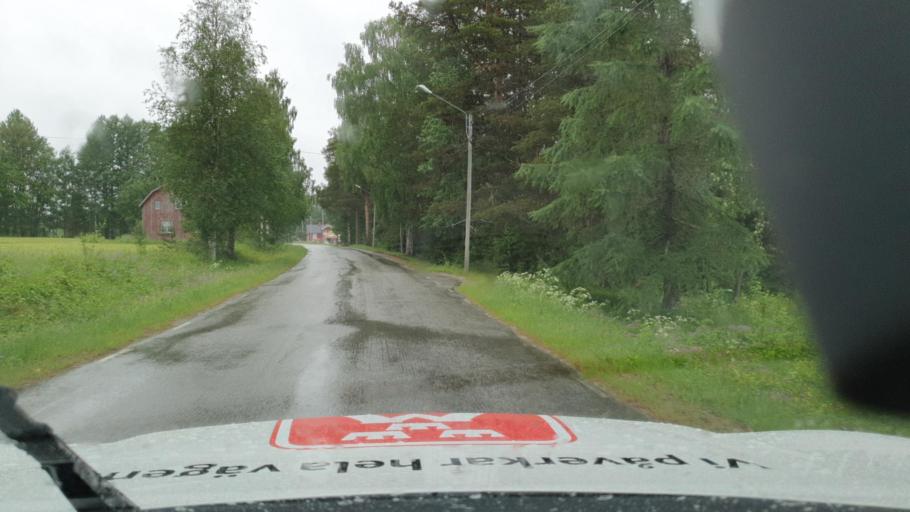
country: SE
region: Vaesterbotten
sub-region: Lycksele Kommun
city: Lycksele
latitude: 64.0754
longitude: 18.3621
